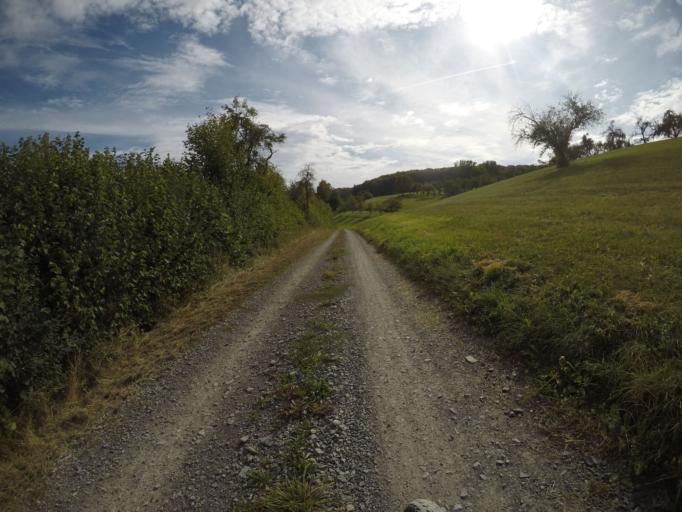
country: DE
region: Baden-Wuerttemberg
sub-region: Regierungsbezirk Stuttgart
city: Eberdingen
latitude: 48.8682
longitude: 8.9653
